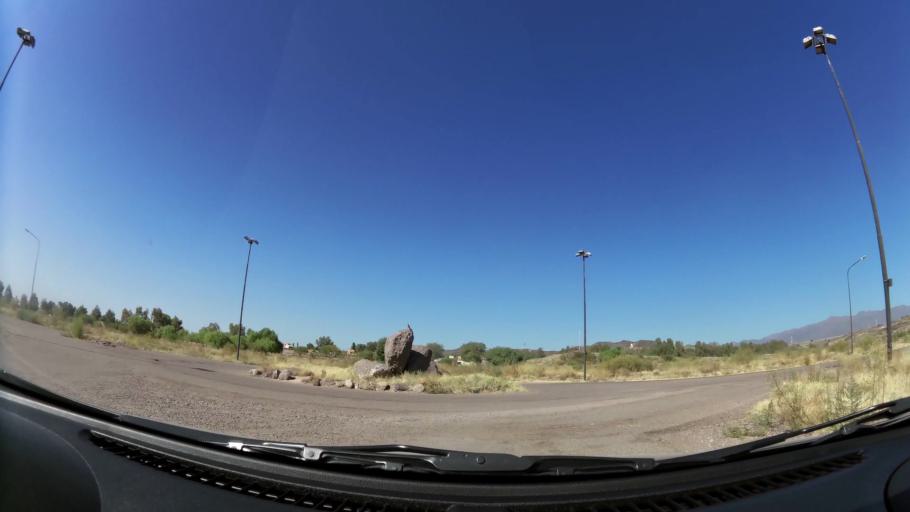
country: AR
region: Mendoza
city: Mendoza
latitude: -32.8975
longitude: -68.8832
